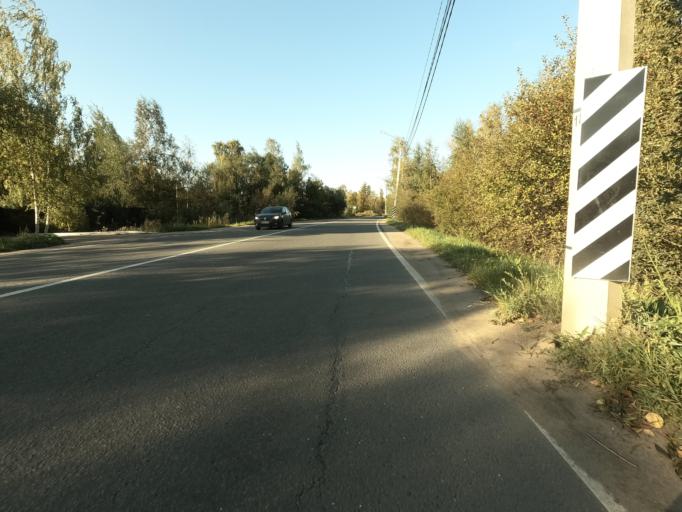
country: RU
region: St.-Petersburg
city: Kolpino
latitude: 59.7543
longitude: 30.6158
